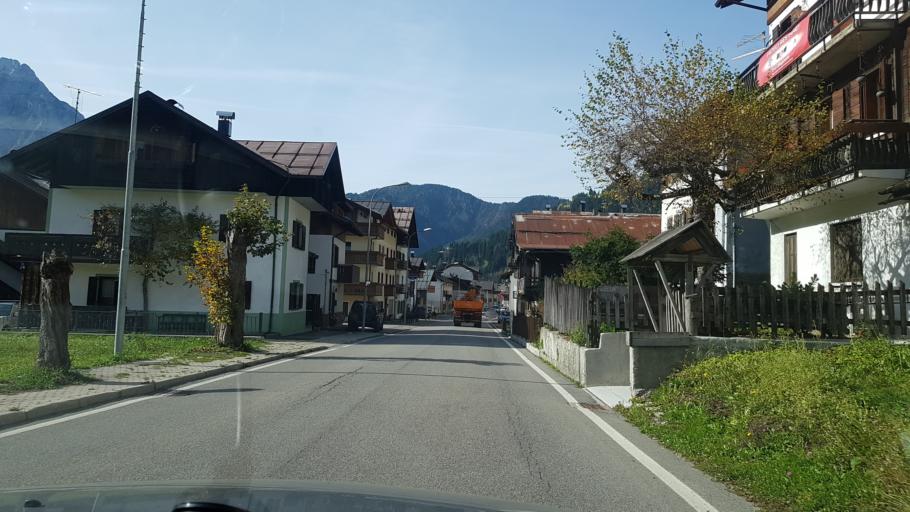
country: IT
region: Veneto
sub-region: Provincia di Belluno
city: Santo Stefano di Cadore
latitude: 46.5597
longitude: 12.5597
